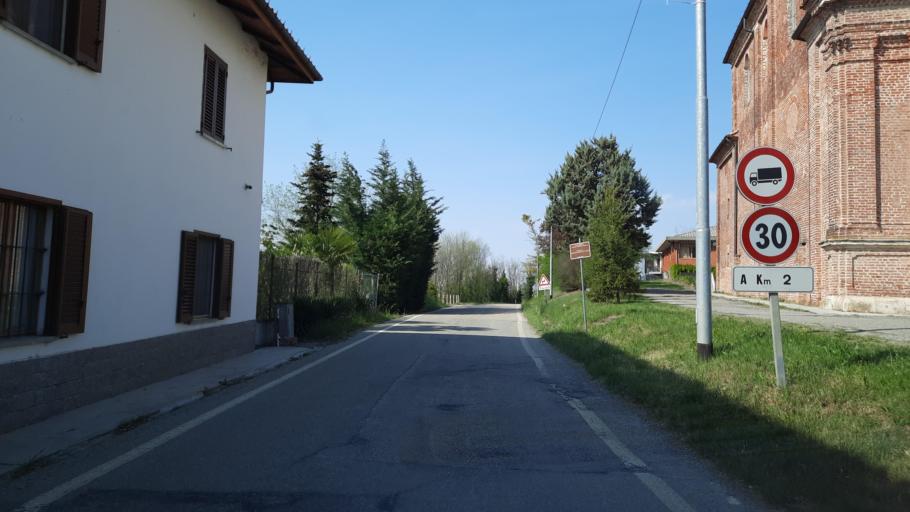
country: IT
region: Piedmont
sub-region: Provincia di Torino
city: Verrua Savoia
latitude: 45.1607
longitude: 8.0959
